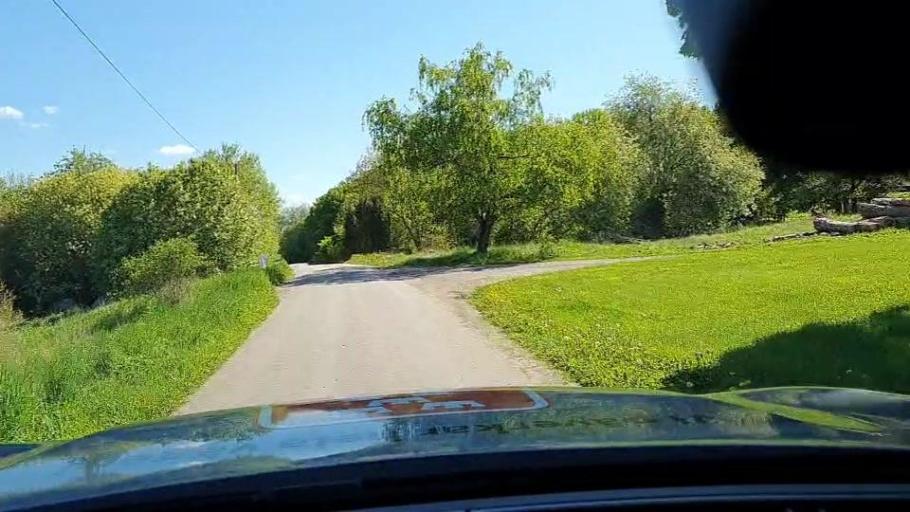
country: SE
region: Soedermanland
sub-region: Strangnas Kommun
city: Strangnas
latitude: 59.4551
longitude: 16.8787
